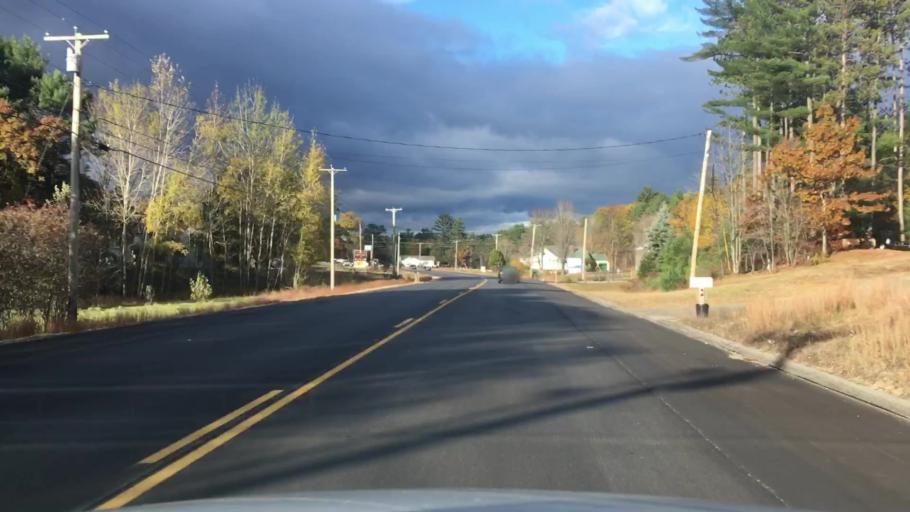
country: US
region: Maine
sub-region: Androscoggin County
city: Livermore
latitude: 44.3642
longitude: -70.2526
